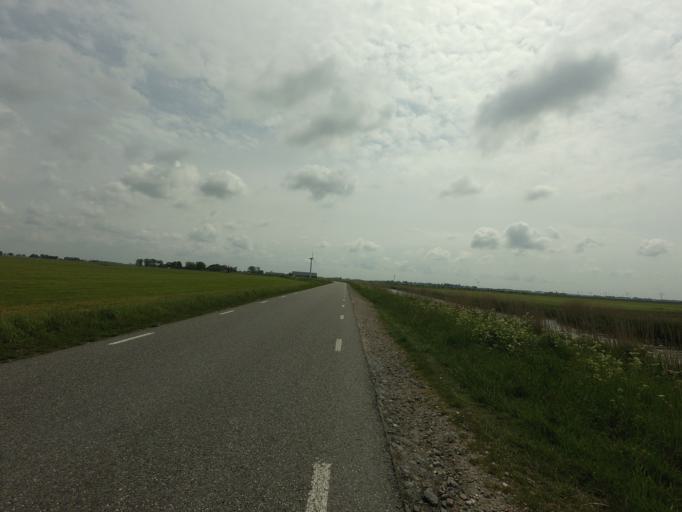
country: NL
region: Friesland
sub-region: Sudwest Fryslan
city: Bolsward
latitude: 53.1026
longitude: 5.5135
